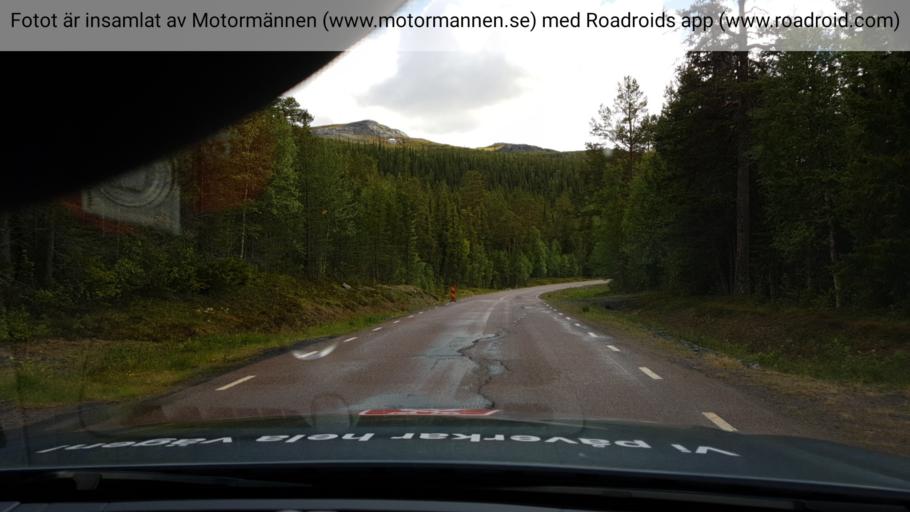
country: SE
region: Jaemtland
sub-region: Are Kommun
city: Jarpen
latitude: 63.0826
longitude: 13.7725
